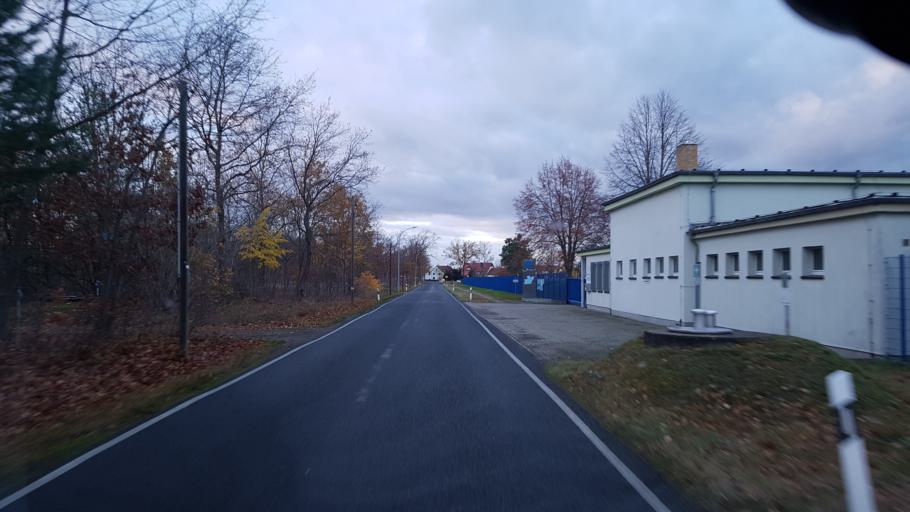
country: DE
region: Brandenburg
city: Tettau
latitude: 51.4268
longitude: 13.7383
